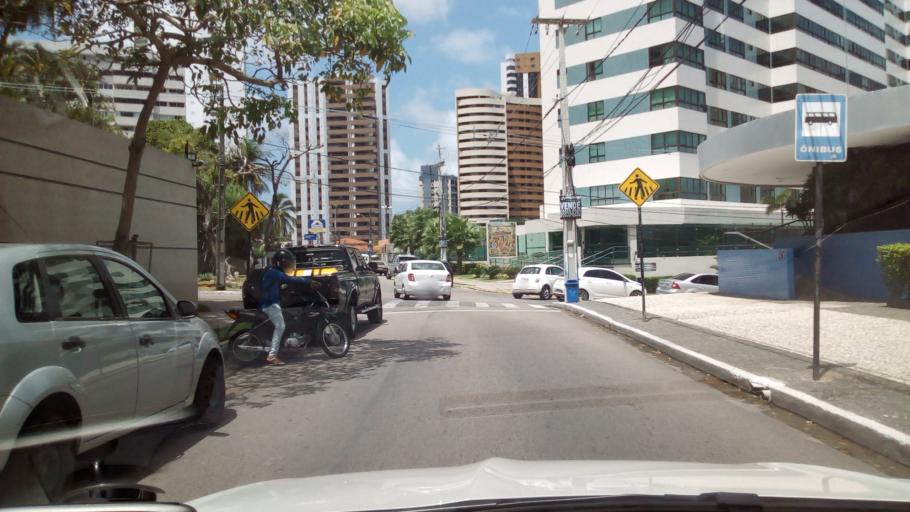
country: BR
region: Paraiba
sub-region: Joao Pessoa
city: Joao Pessoa
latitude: -7.1177
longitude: -34.8361
